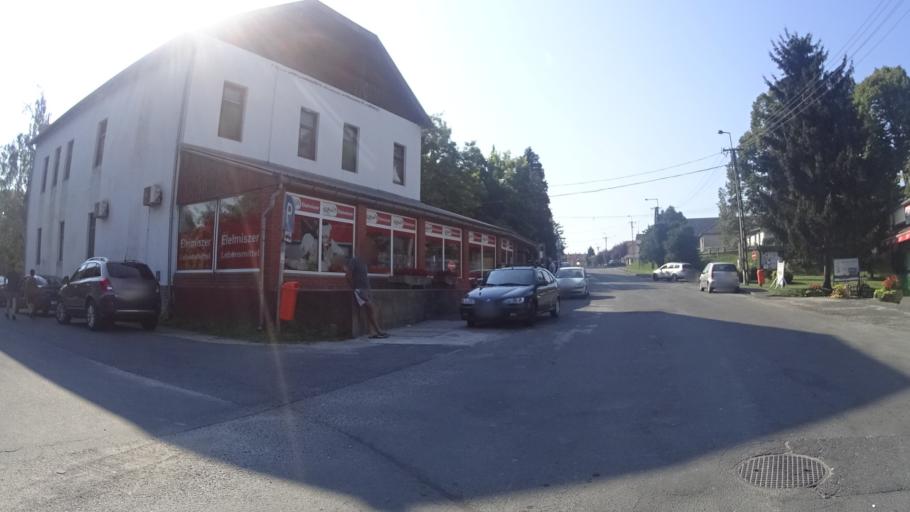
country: HU
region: Somogy
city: Balatonbereny
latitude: 46.7135
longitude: 17.3173
